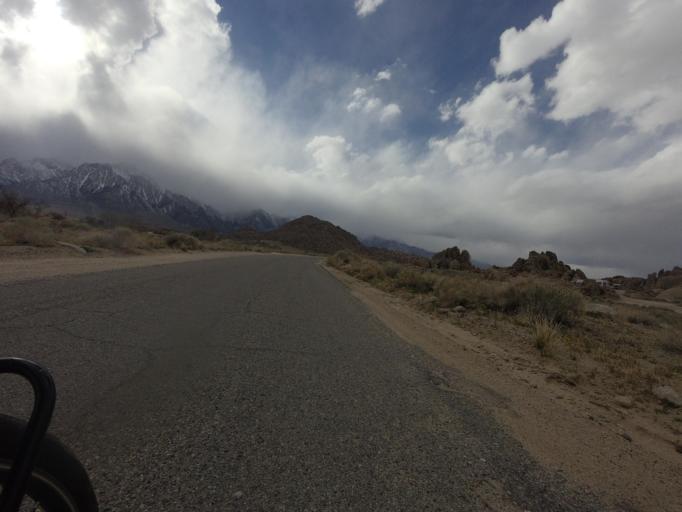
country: US
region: California
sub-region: Inyo County
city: Lone Pine
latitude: 36.5978
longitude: -118.1137
